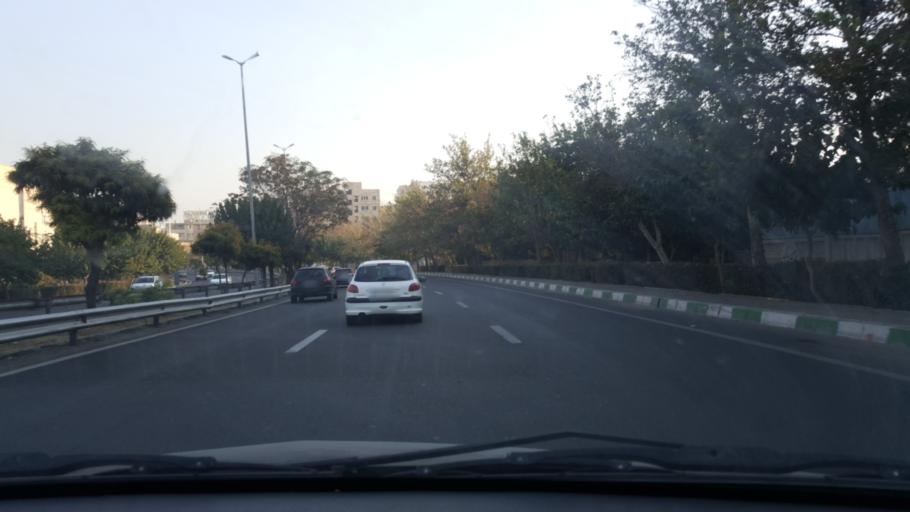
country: IR
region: Tehran
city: Tehran
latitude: 35.7351
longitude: 51.2846
